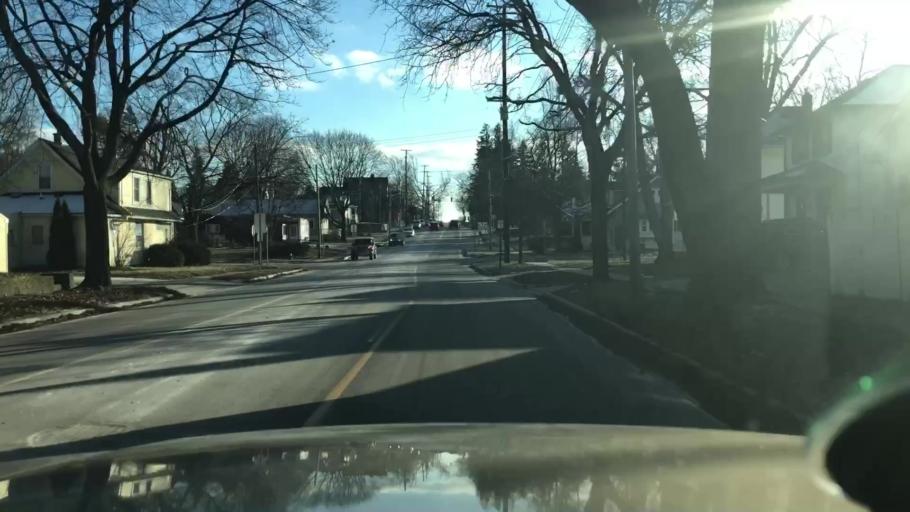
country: US
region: Michigan
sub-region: Jackson County
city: Jackson
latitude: 42.2316
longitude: -84.4233
